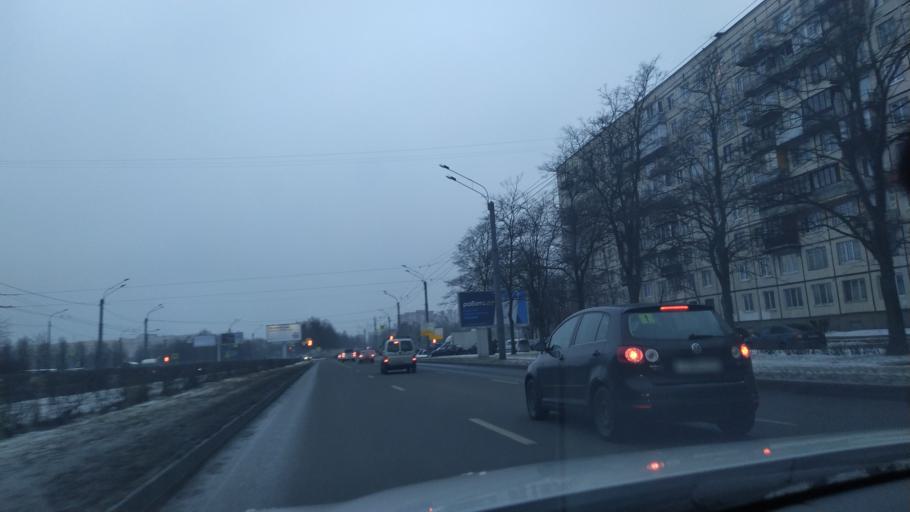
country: RU
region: St.-Petersburg
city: Grazhdanka
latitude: 60.0324
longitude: 30.3927
